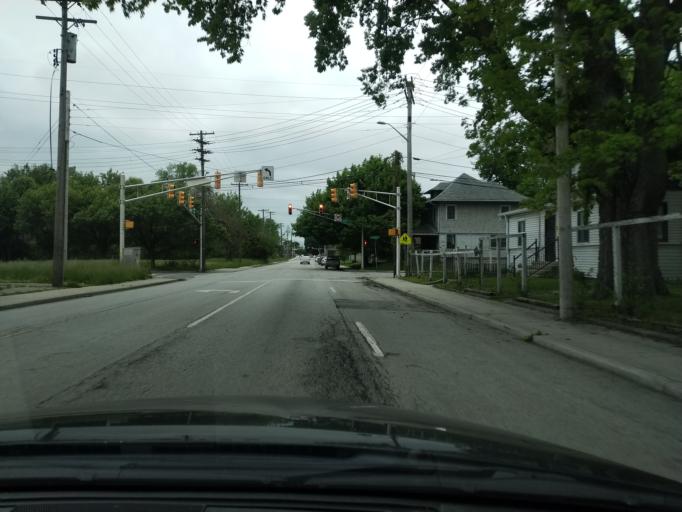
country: US
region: Indiana
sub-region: Marion County
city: Indianapolis
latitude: 39.8089
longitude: -86.1496
